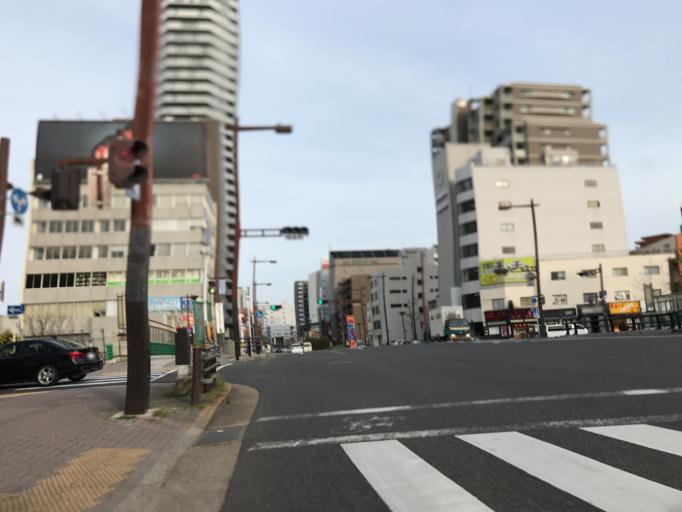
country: JP
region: Aichi
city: Nagoya-shi
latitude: 35.1729
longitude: 136.9325
